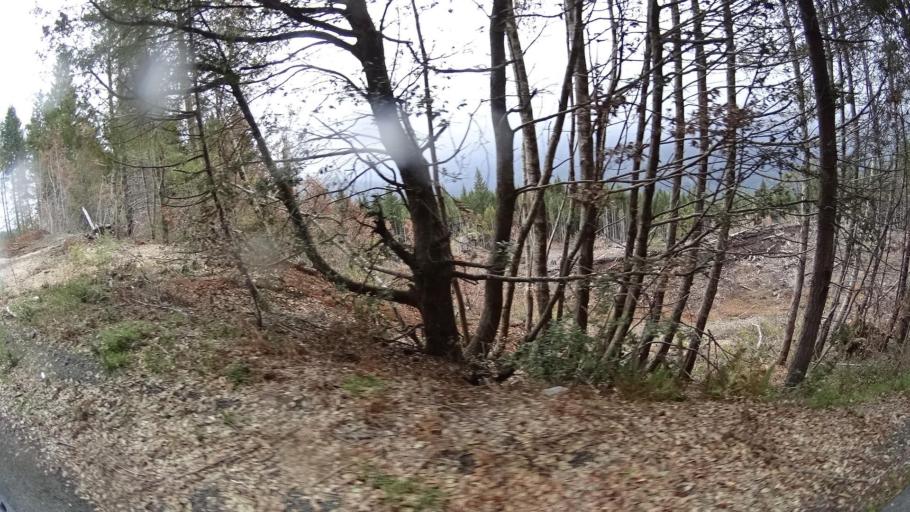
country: US
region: California
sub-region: Humboldt County
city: Willow Creek
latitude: 41.2019
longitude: -123.7886
